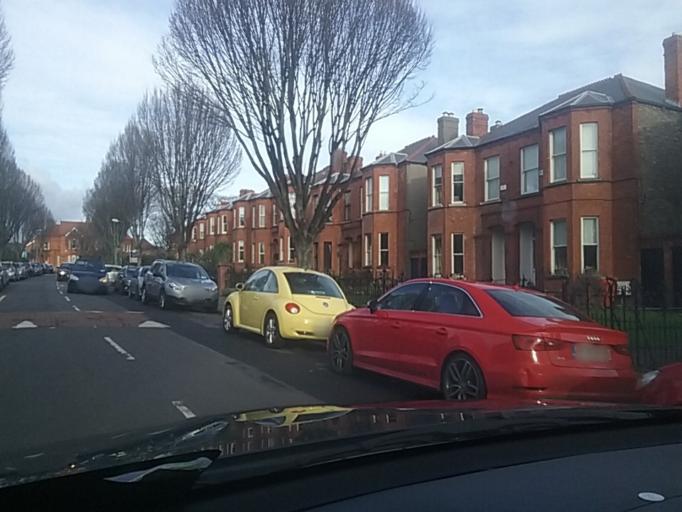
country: IE
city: Donnycarney
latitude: 53.3654
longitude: -6.2178
